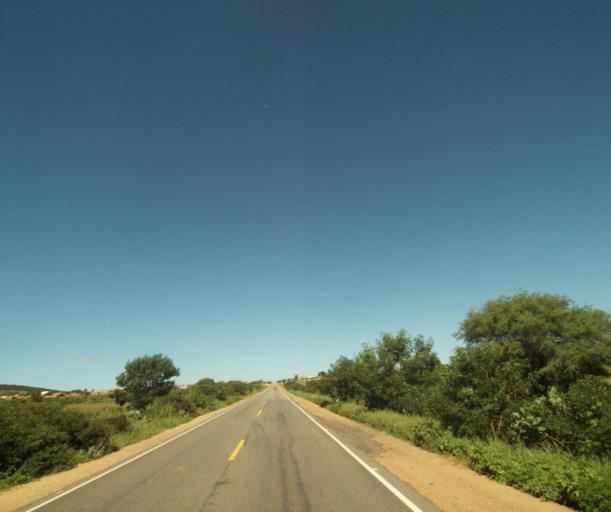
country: BR
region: Bahia
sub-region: Palmas De Monte Alto
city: Palmas de Monte Alto
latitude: -14.2495
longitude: -43.1623
